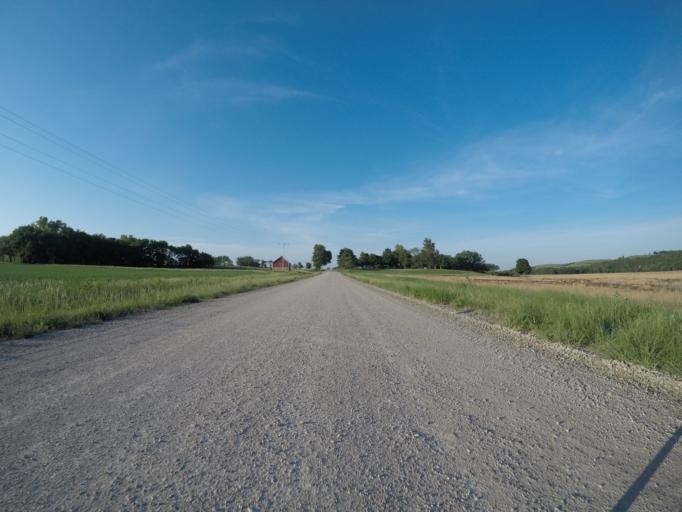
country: US
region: Kansas
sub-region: Riley County
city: Manhattan
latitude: 39.1141
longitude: -96.4878
